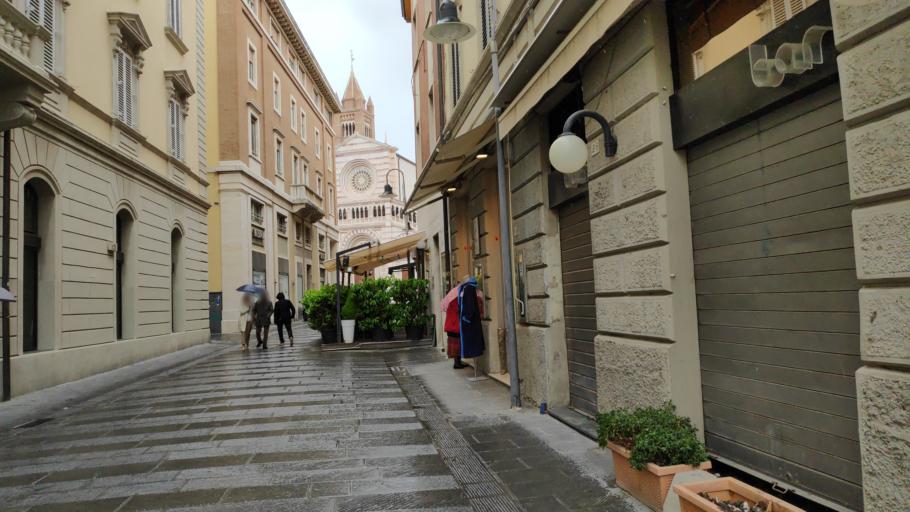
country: IT
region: Tuscany
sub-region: Provincia di Grosseto
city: Grosseto
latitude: 42.7597
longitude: 11.1127
